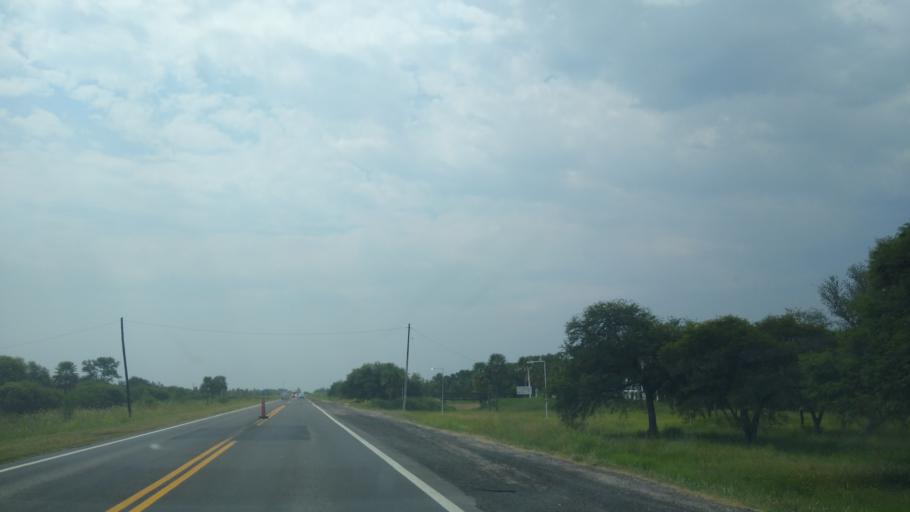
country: AR
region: Chaco
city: Margarita Belen
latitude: -27.1167
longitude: -58.9701
